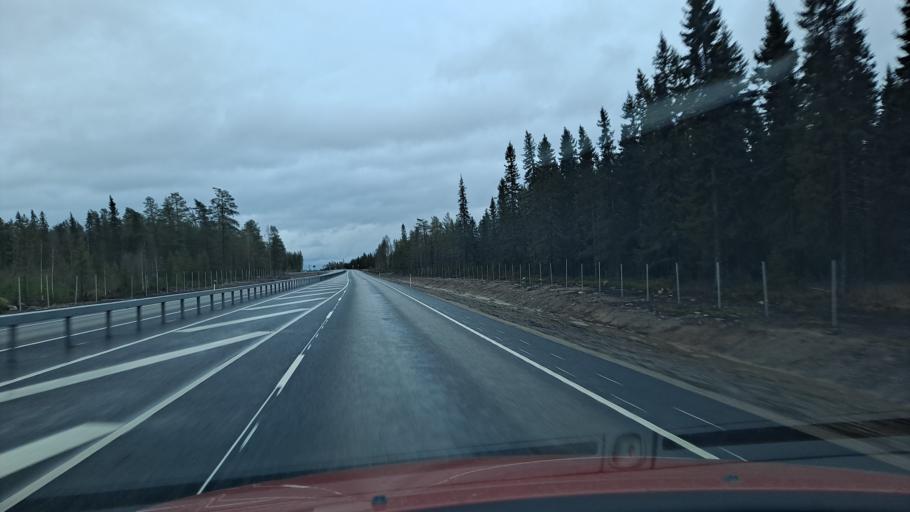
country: FI
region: Lapland
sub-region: Kemi-Tornio
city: Simo
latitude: 65.6343
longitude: 25.1187
